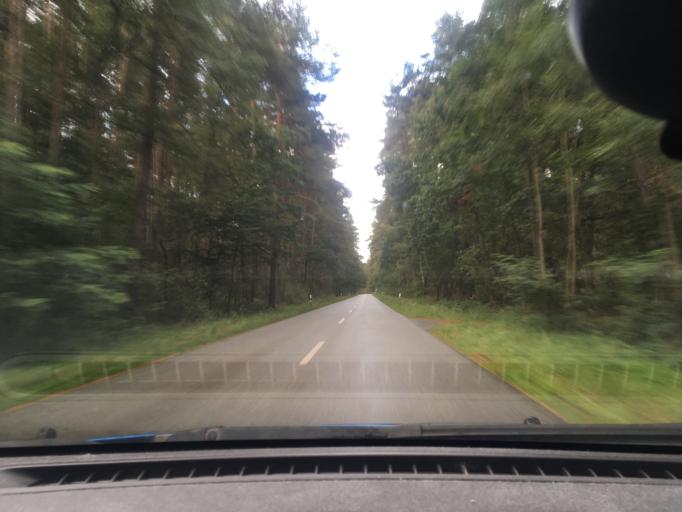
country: DE
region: Lower Saxony
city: Neu Darchau
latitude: 53.3143
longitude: 10.9107
